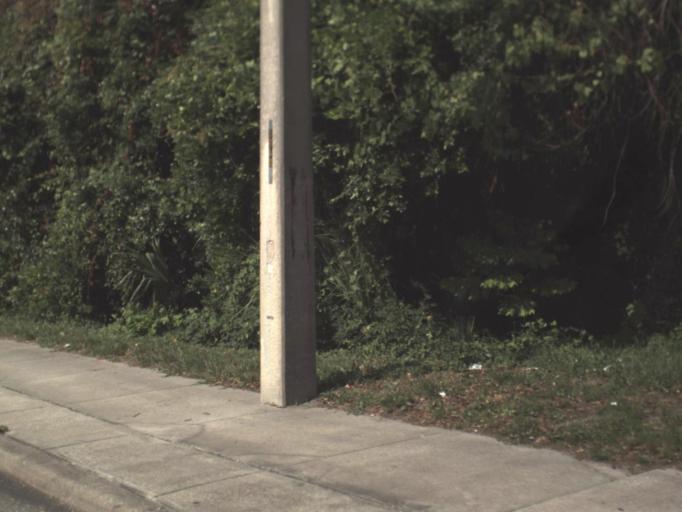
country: US
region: Florida
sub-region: Duval County
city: Jacksonville
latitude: 30.2876
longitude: -81.7554
